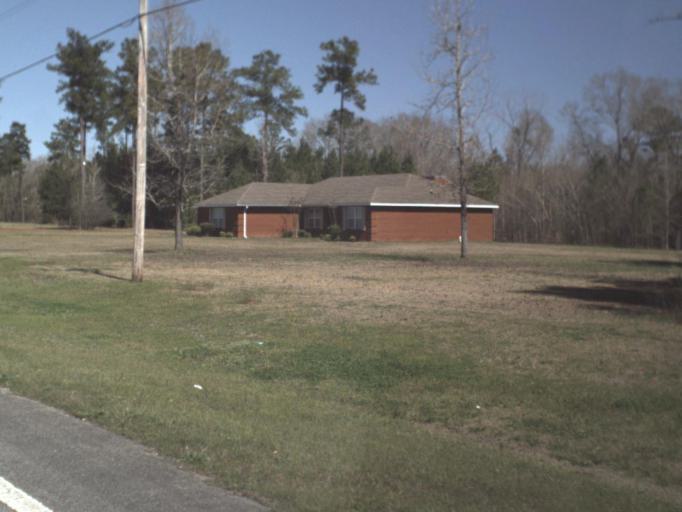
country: US
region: Florida
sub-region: Gadsden County
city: Quincy
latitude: 30.6318
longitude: -84.5989
